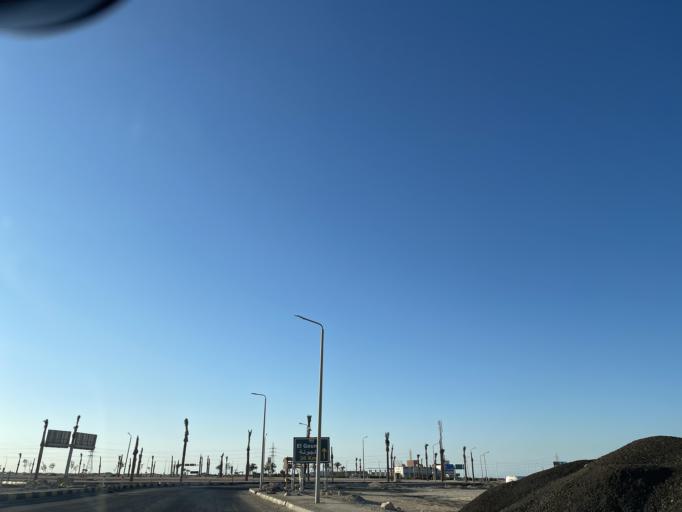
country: EG
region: Red Sea
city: Hurghada
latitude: 27.2297
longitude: 33.7814
